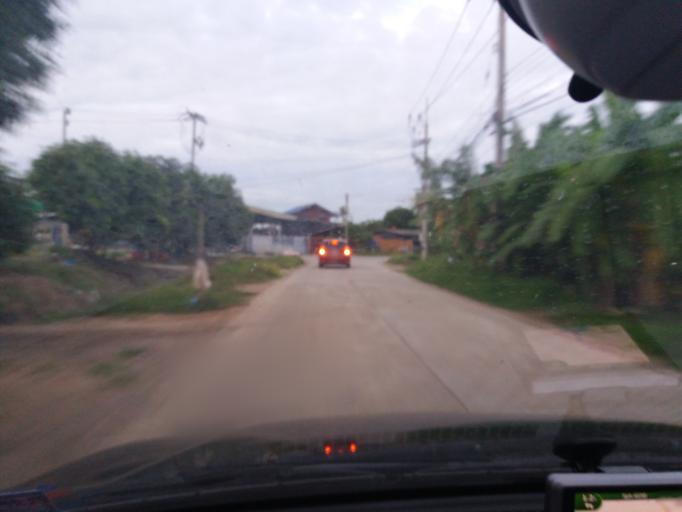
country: TH
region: Suphan Buri
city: Ban Sam Chuk
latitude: 14.7220
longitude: 100.0717
